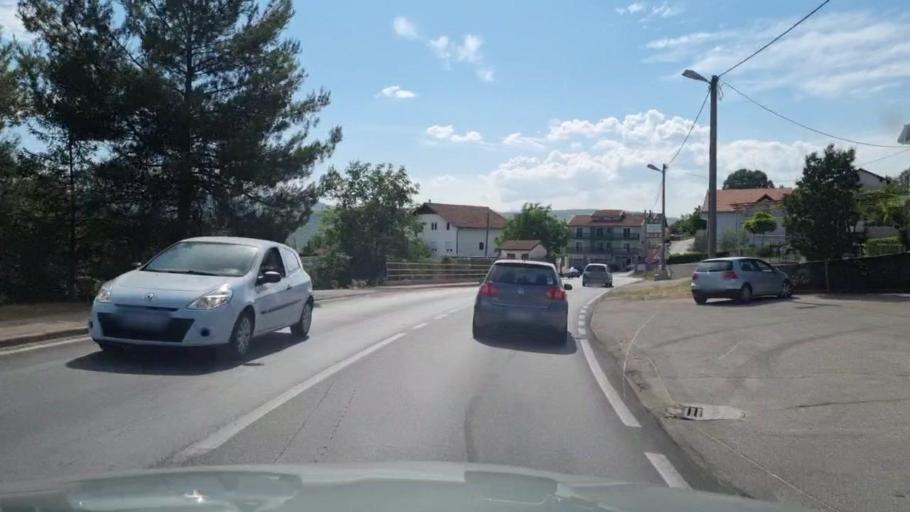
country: BA
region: Federation of Bosnia and Herzegovina
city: Grude
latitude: 43.3683
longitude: 17.4271
